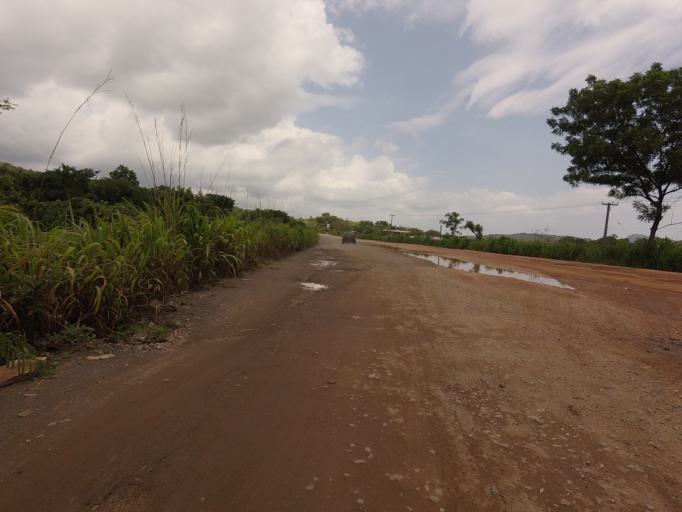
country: GH
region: Volta
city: Ho
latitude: 6.6769
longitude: 0.3144
